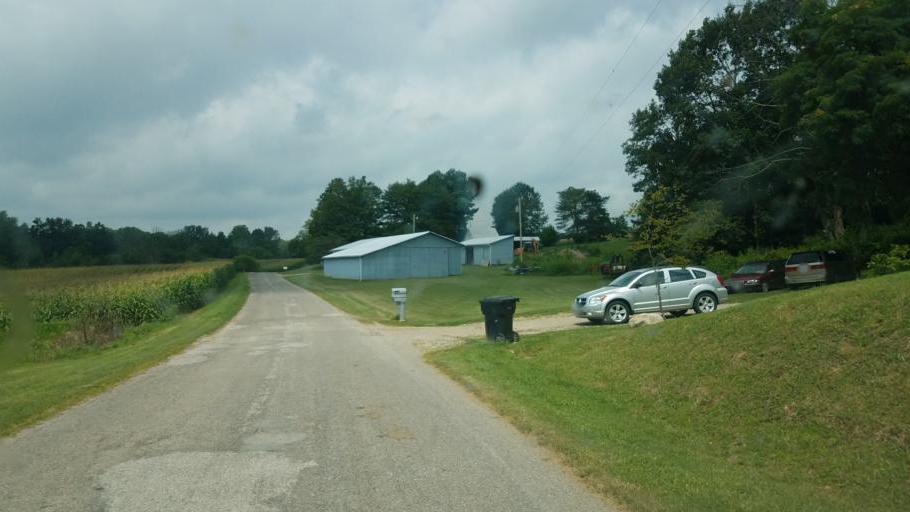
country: US
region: Ohio
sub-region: Morrow County
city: Mount Gilead
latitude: 40.5296
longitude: -82.6964
